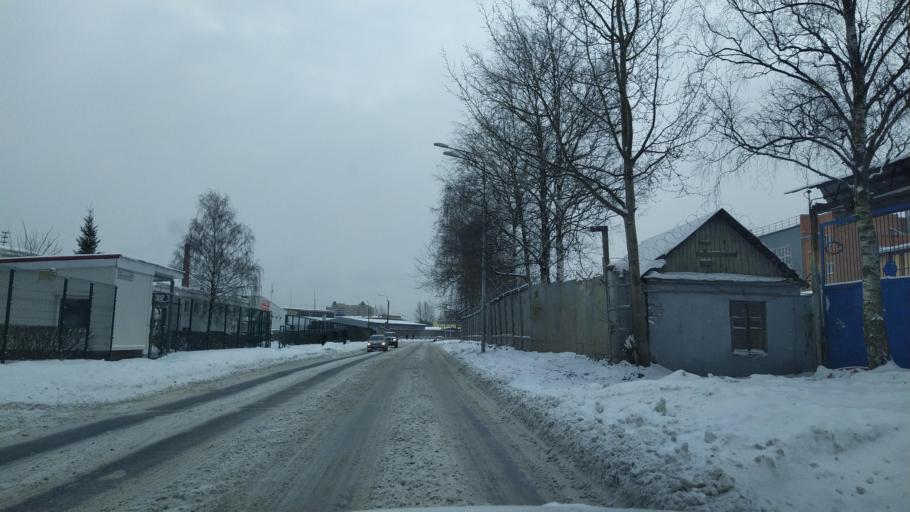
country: RU
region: St.-Petersburg
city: Novaya Derevnya
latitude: 59.9925
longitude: 30.2766
